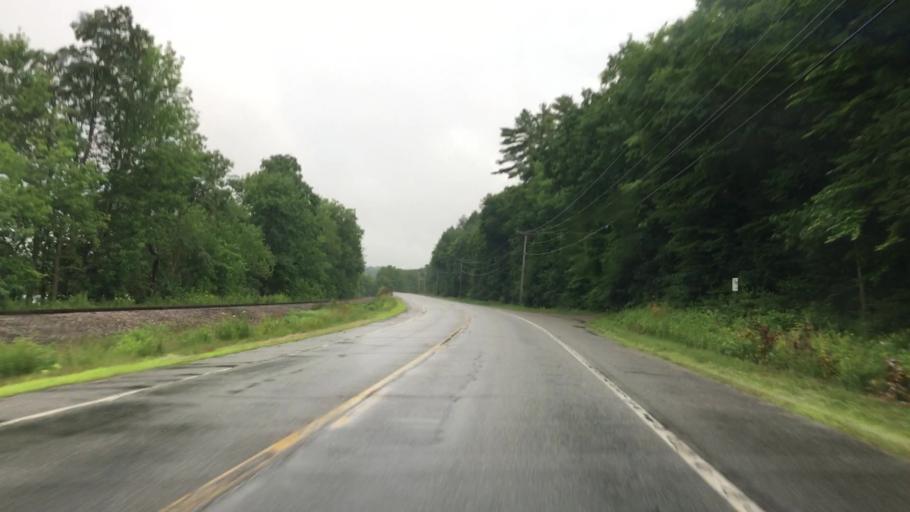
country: US
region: Maine
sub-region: Kennebec County
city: Pittston
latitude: 44.2021
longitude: -69.7644
